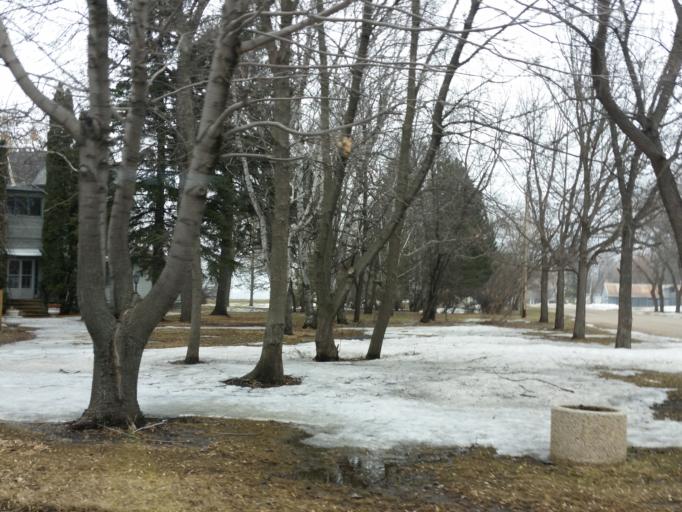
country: US
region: North Dakota
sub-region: Walsh County
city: Grafton
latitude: 48.6224
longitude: -97.4490
